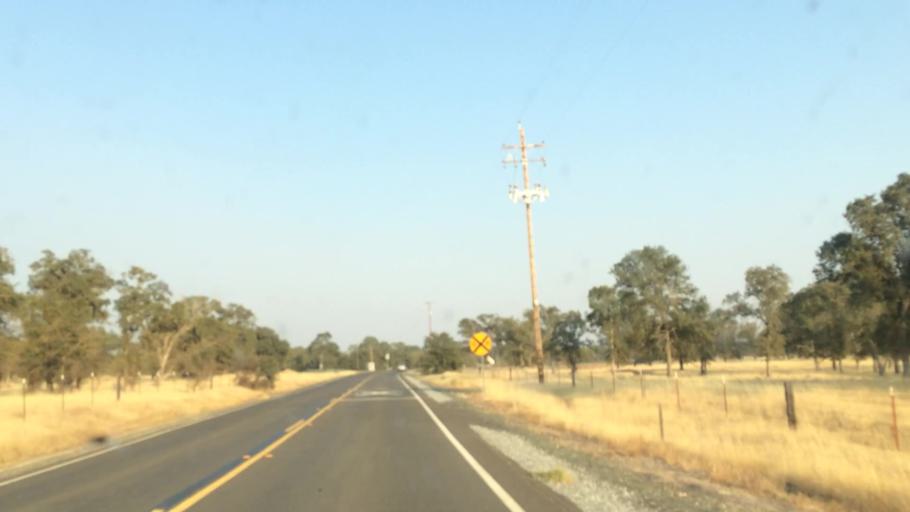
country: US
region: California
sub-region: Amador County
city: Ione
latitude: 38.3940
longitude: -120.9998
